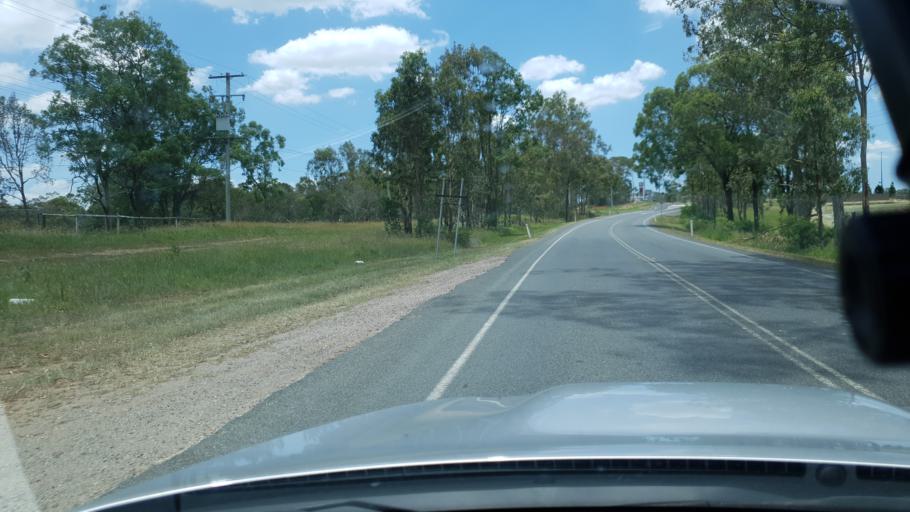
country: AU
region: Queensland
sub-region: Logan
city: North Maclean
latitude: -27.7419
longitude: 152.9848
